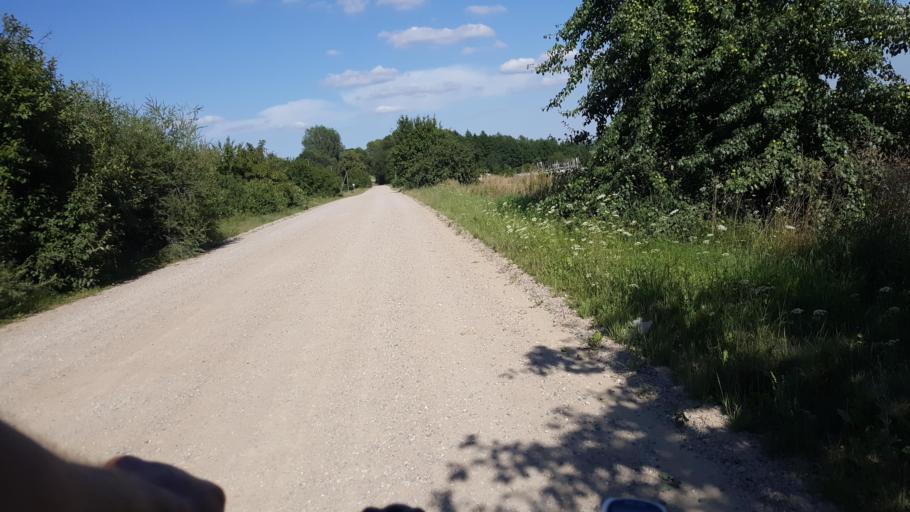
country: BY
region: Brest
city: Charnawchytsy
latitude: 52.3415
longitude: 23.6510
